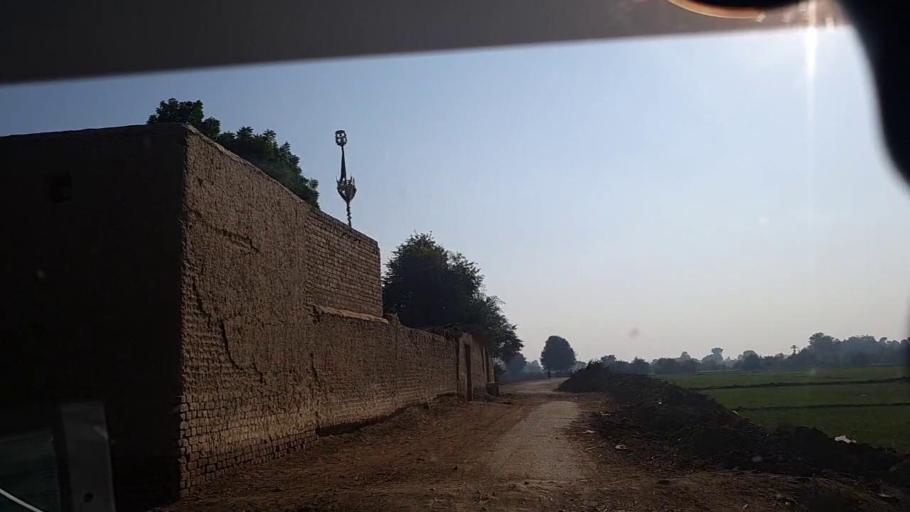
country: PK
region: Sindh
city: Hingorja
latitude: 27.2183
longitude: 68.2660
